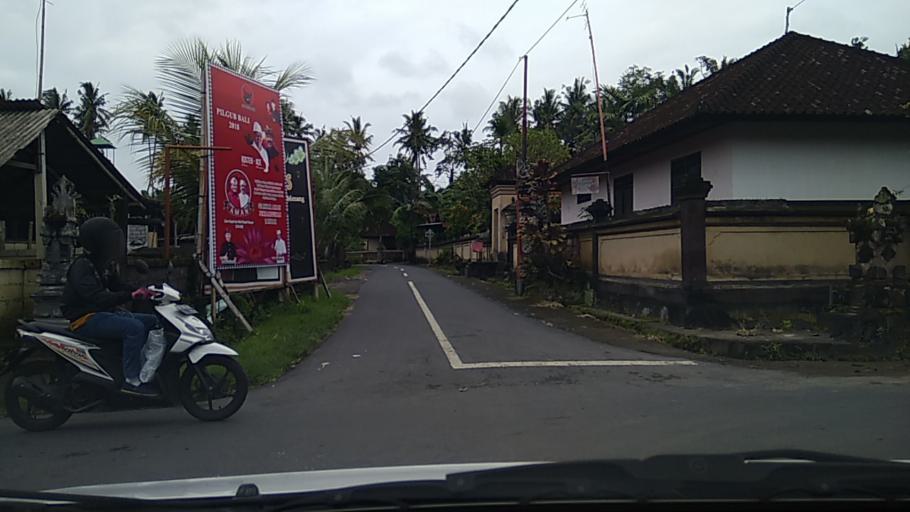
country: ID
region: Bali
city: Banjar Tebongkang
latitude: -8.5269
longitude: 115.2391
